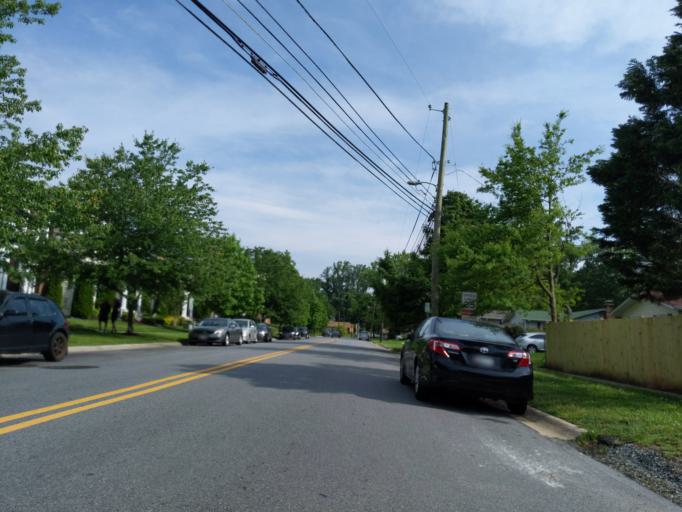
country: US
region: Maryland
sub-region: Montgomery County
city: Wheaton
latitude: 39.0452
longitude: -77.0481
